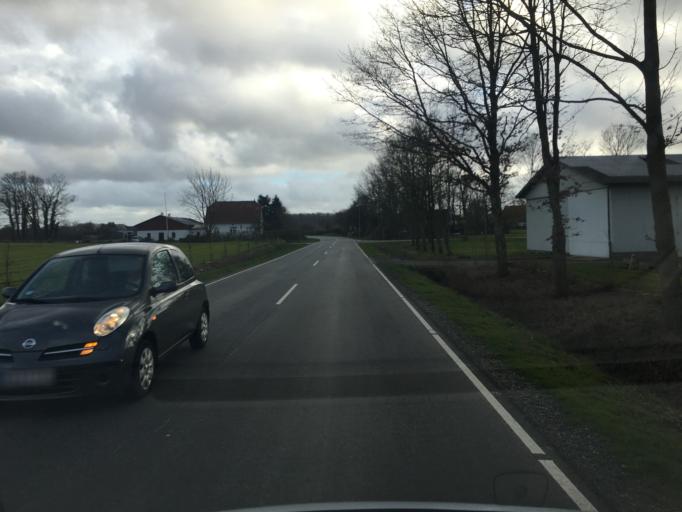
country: DE
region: Schleswig-Holstein
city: Wees
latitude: 54.8938
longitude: 9.4918
